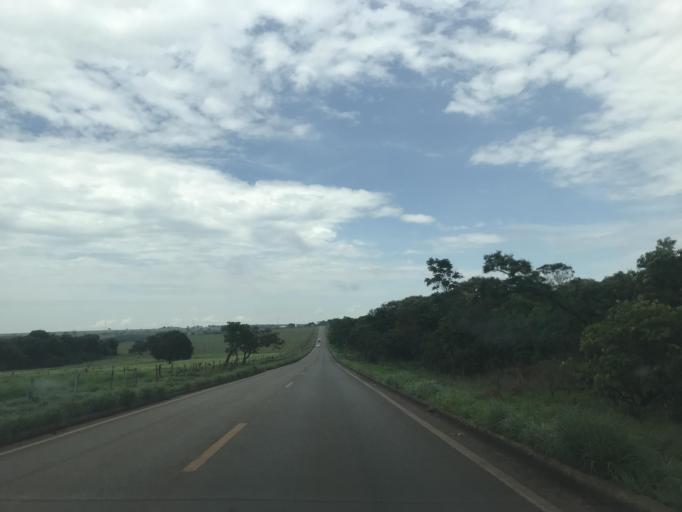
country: BR
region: Goias
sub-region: Luziania
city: Luziania
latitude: -16.2690
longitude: -47.9840
